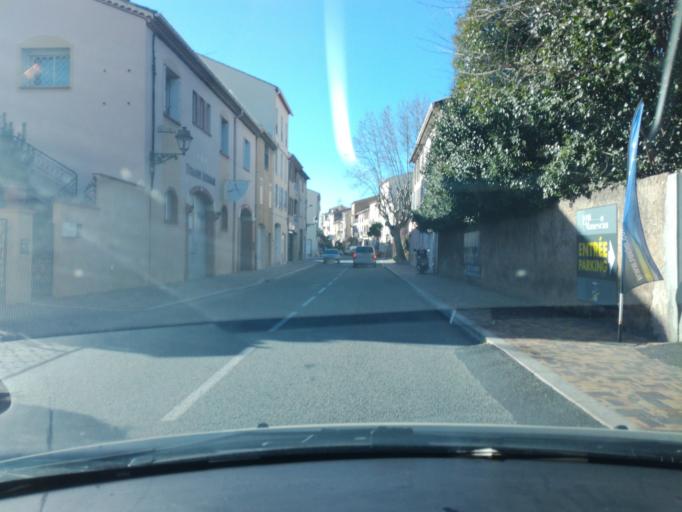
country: FR
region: Provence-Alpes-Cote d'Azur
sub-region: Departement du Var
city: Puget-sur-Argens
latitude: 43.4544
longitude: 6.6881
